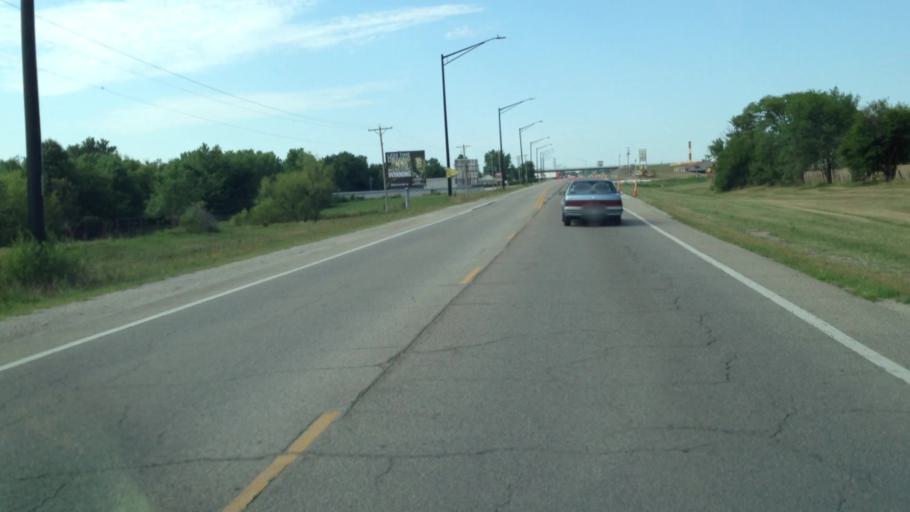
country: US
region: Kansas
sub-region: Labette County
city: Parsons
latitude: 37.3600
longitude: -95.2586
